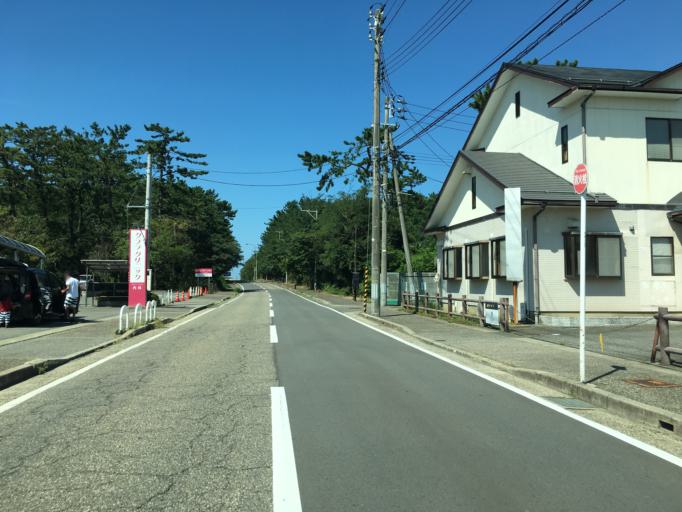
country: JP
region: Niigata
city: Niigata-shi
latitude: 37.8996
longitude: 138.9939
